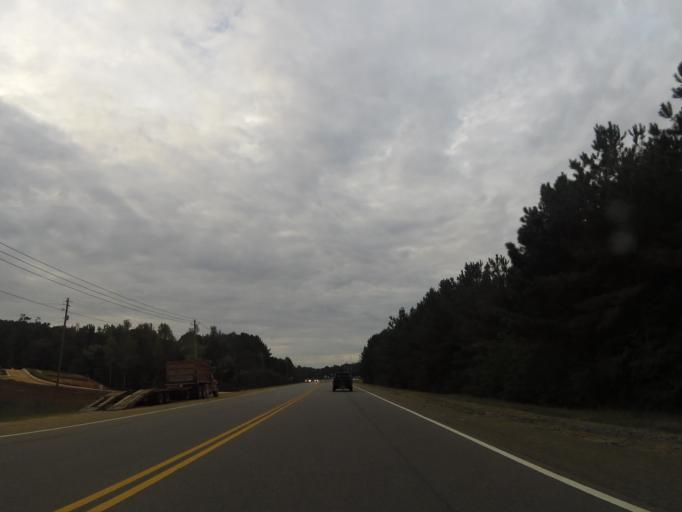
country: US
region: Alabama
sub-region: Jefferson County
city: Trussville
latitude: 33.6541
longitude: -86.5760
